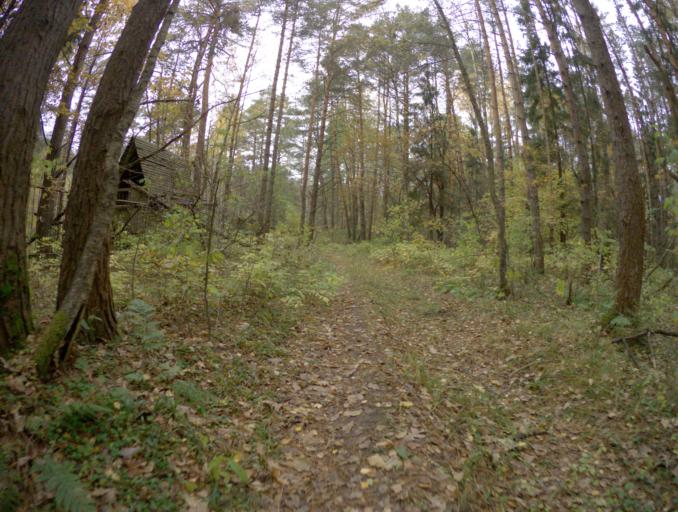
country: RU
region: Vladimir
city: Kommunar
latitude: 56.0724
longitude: 40.4480
